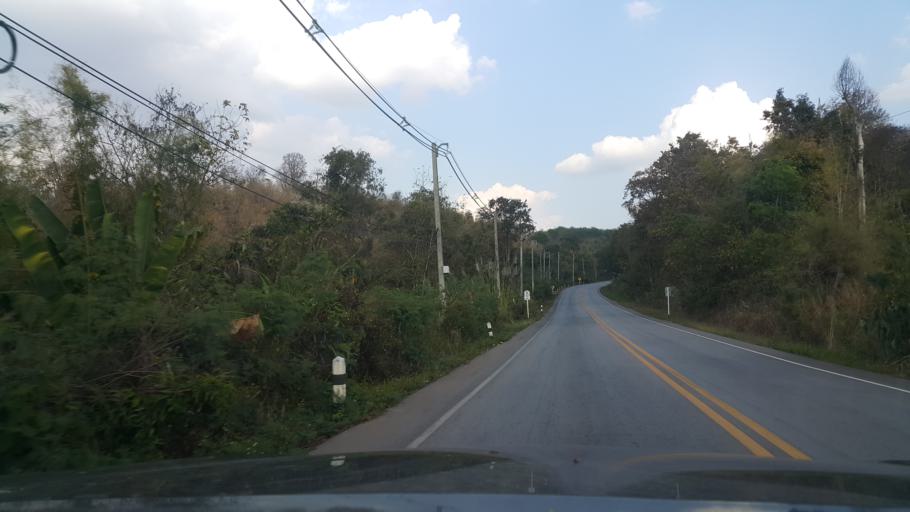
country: TH
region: Loei
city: Dan Sai
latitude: 17.2499
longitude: 101.1143
